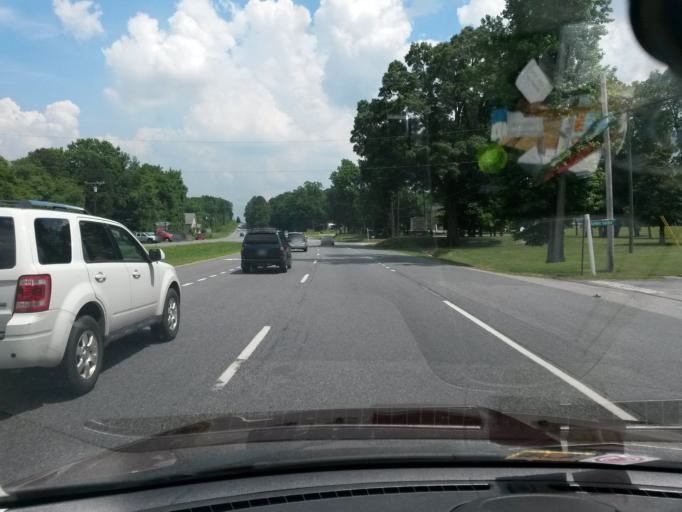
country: US
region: Virginia
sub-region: Chesterfield County
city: Enon
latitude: 37.3266
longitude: -77.3185
